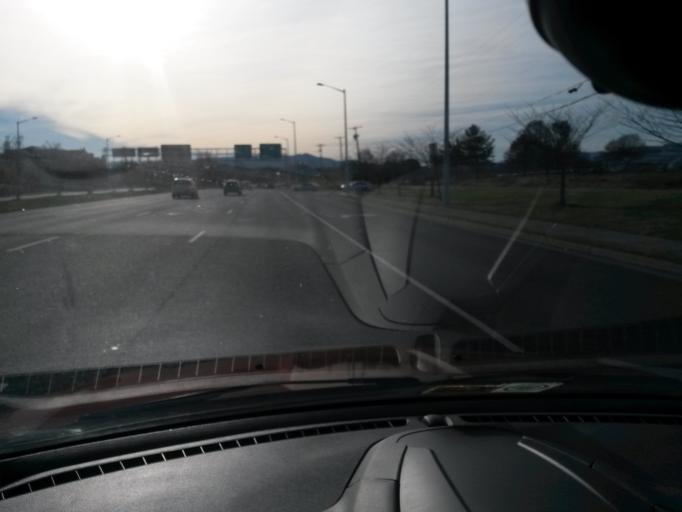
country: US
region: Virginia
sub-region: Roanoke County
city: Hollins
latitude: 37.3117
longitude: -79.9688
